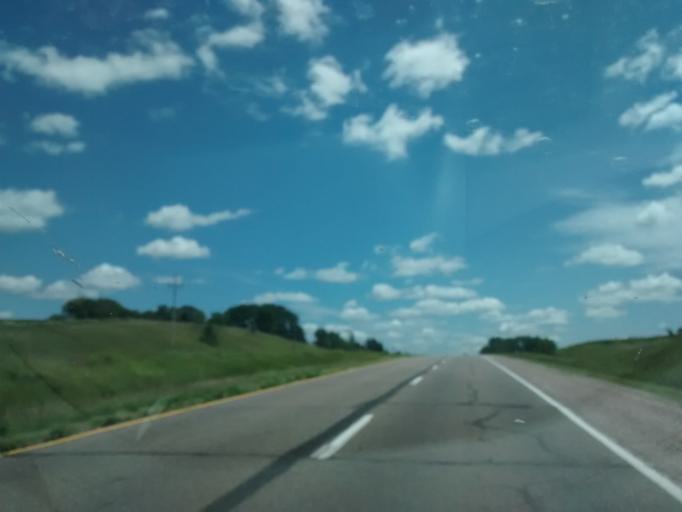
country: US
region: Iowa
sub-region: Woodbury County
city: Moville
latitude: 42.4748
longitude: -96.1234
